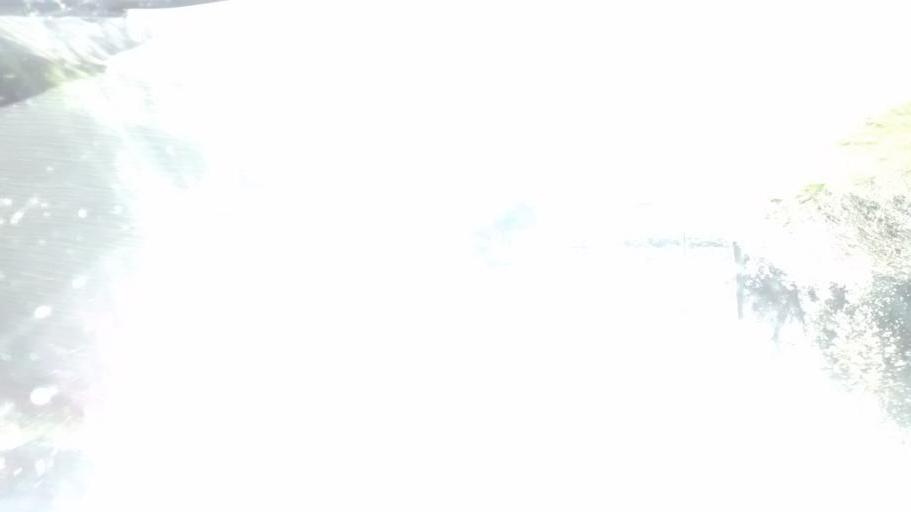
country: FR
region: Brittany
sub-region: Departement d'Ille-et-Vilaine
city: La Bouexiere
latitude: 48.2058
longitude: -1.4591
